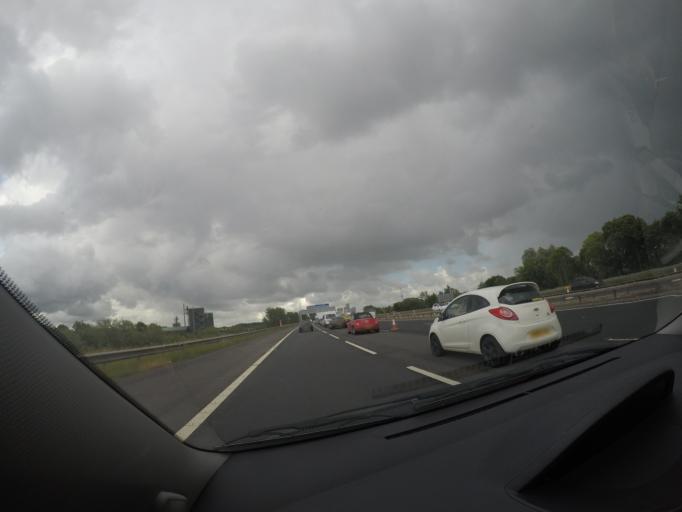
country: GB
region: Scotland
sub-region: South Lanarkshire
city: Uddingston
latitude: 55.8226
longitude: -4.0733
